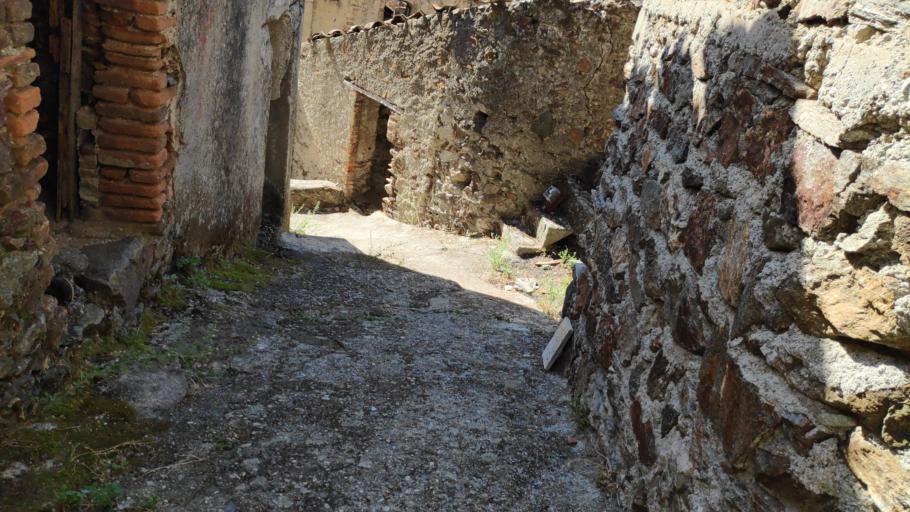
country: IT
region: Calabria
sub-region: Provincia di Reggio Calabria
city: Roccaforte del Greco
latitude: 38.0486
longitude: 15.9166
